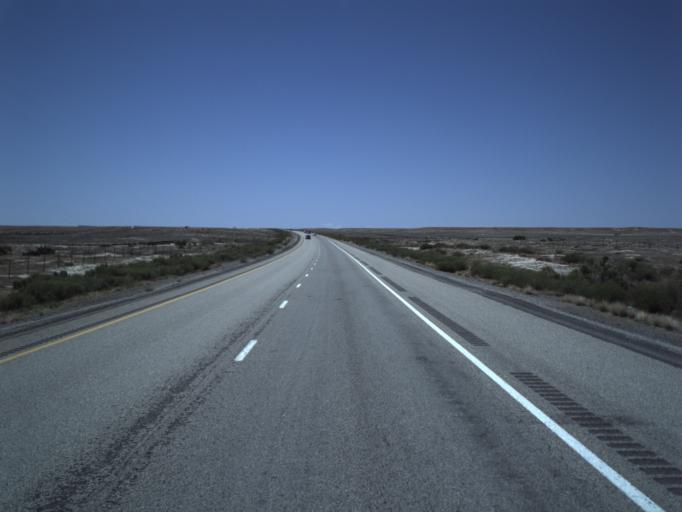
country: US
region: Utah
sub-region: Grand County
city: Moab
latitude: 38.9680
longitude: -109.3702
